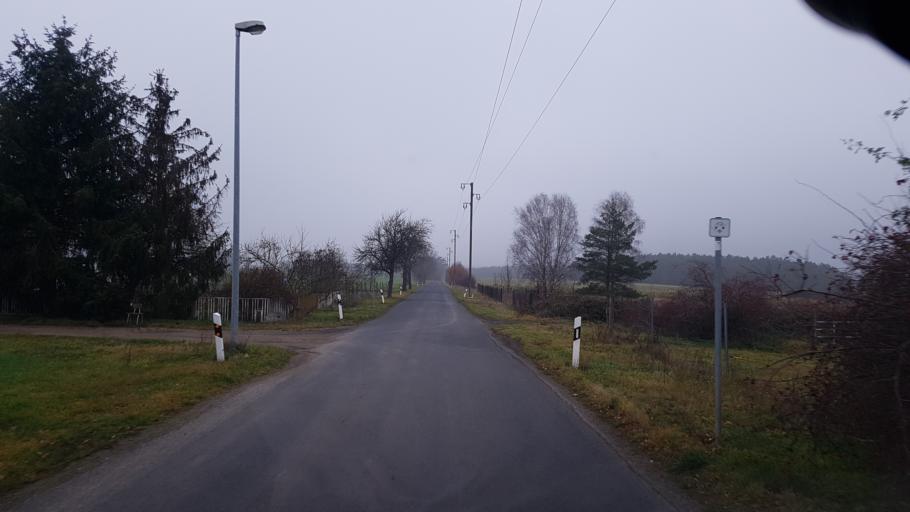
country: DE
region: Brandenburg
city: Altdobern
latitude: 51.6775
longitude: 13.9853
